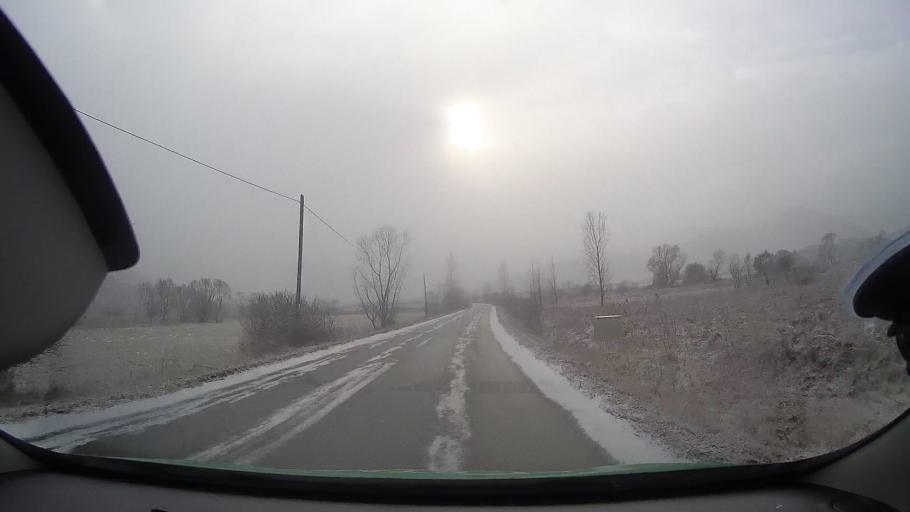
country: RO
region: Alba
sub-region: Comuna Rimetea
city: Rimetea
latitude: 46.4042
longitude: 23.5574
